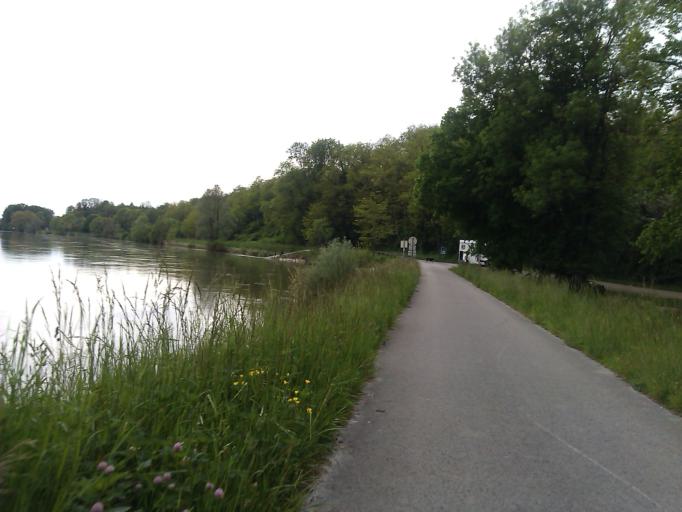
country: FR
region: Franche-Comte
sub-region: Departement du Jura
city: Dampierre
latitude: 47.1516
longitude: 5.7387
